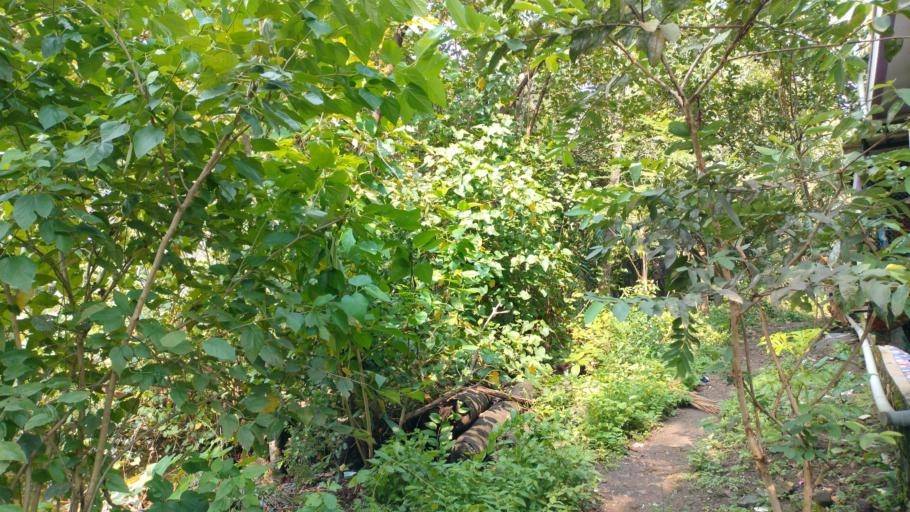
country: IN
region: Maharashtra
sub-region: Thane
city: Virar
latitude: 19.4291
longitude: 72.7903
